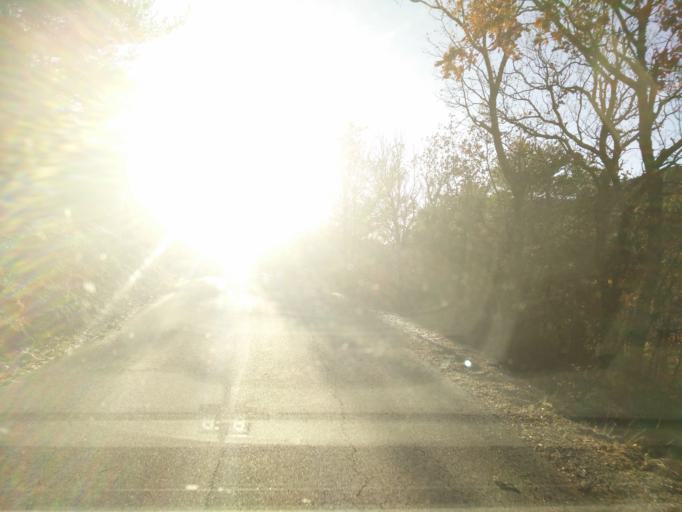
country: FR
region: Provence-Alpes-Cote d'Azur
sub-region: Departement des Alpes-de-Haute-Provence
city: Castellane
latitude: 43.7897
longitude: 6.3768
